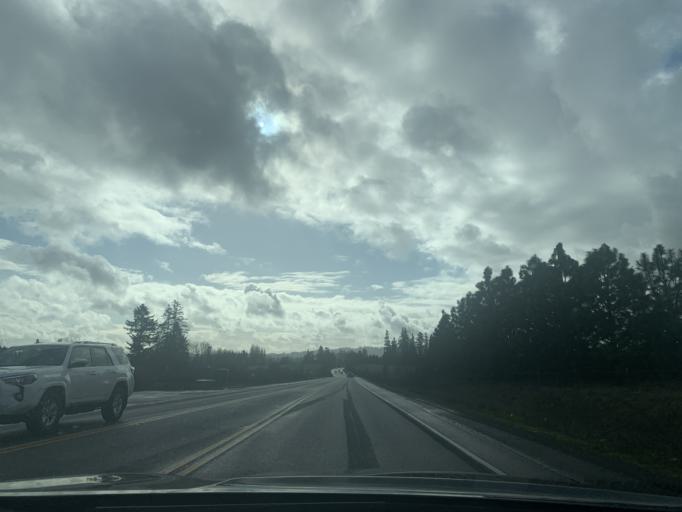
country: US
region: Oregon
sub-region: Washington County
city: Sherwood
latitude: 45.3972
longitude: -122.8520
